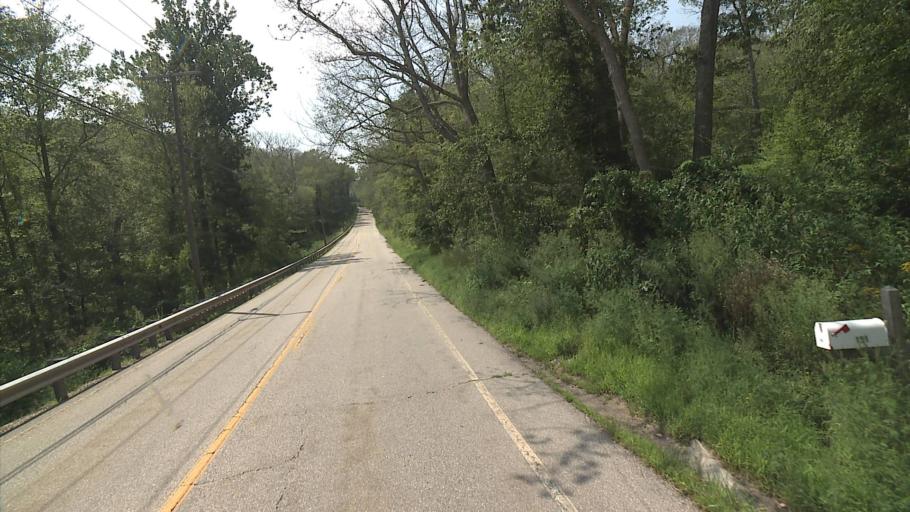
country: US
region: Connecticut
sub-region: Middlesex County
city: Essex Village
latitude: 41.4338
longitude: -72.3452
